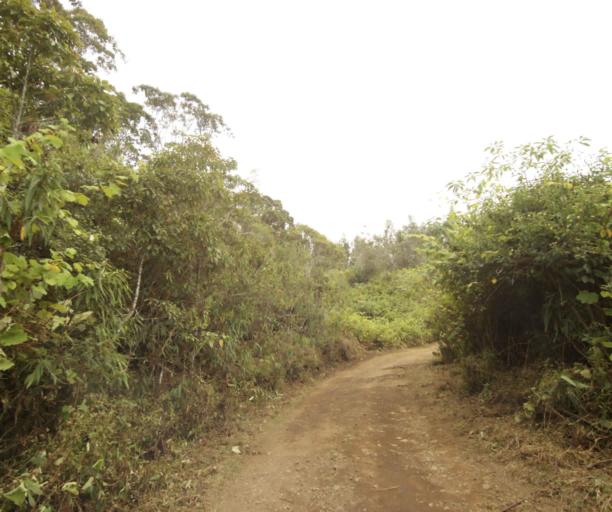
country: RE
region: Reunion
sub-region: Reunion
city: La Possession
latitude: -21.0128
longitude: 55.3599
